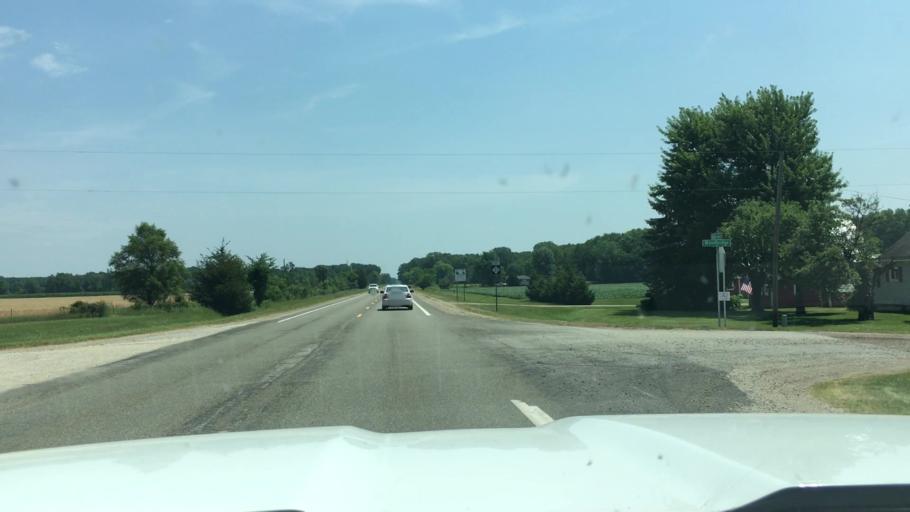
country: US
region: Michigan
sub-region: Clinton County
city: Ovid
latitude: 43.1759
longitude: -84.4083
